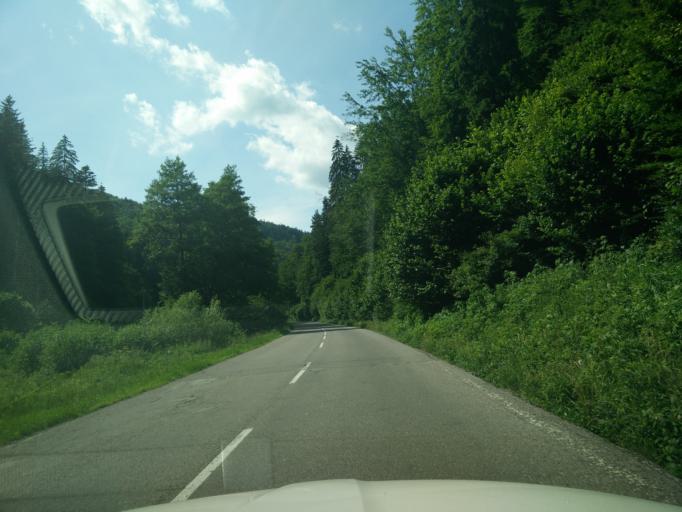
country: SK
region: Nitriansky
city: Bojnice
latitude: 48.9313
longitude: 18.6380
